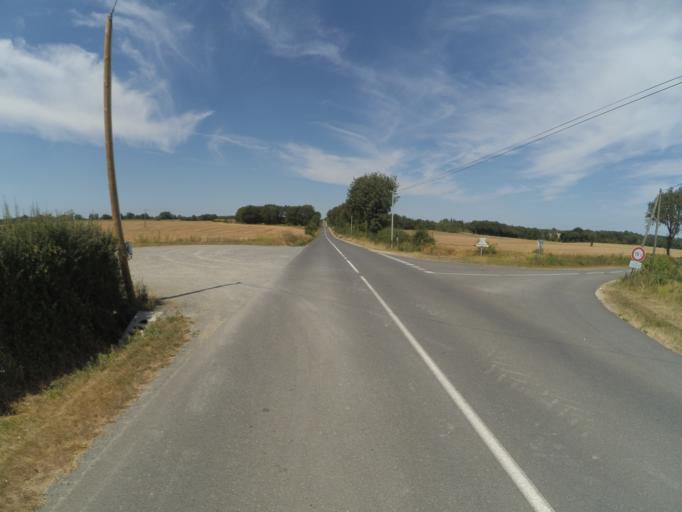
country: FR
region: Poitou-Charentes
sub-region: Departement de la Vienne
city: Usson-du-Poitou
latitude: 46.2324
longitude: 0.5280
